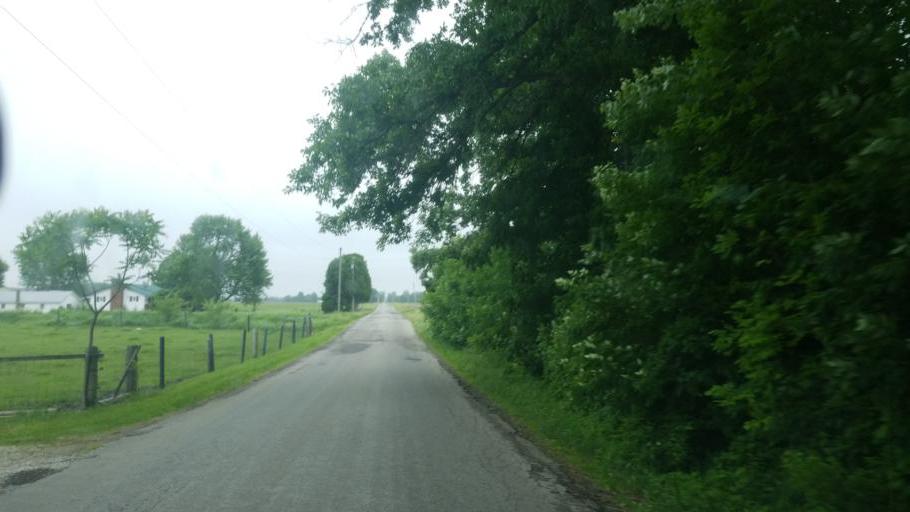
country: US
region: Indiana
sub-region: Marshall County
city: Bremen
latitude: 41.4773
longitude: -86.1178
